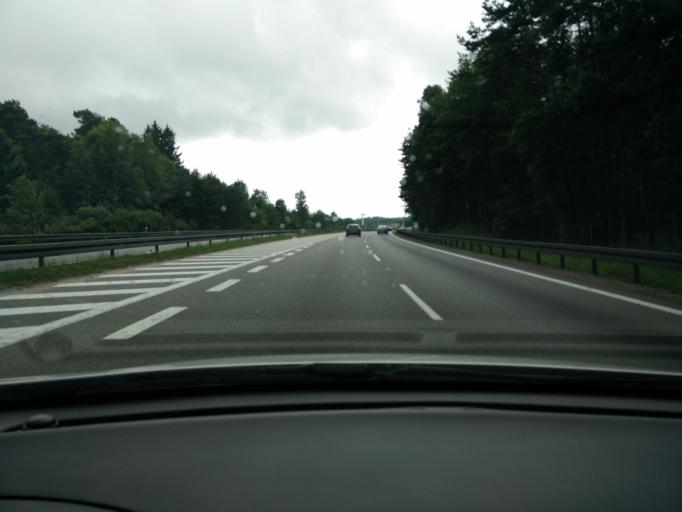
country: PL
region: Pomeranian Voivodeship
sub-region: Gdynia
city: Wielki Kack
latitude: 54.4809
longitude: 18.4726
